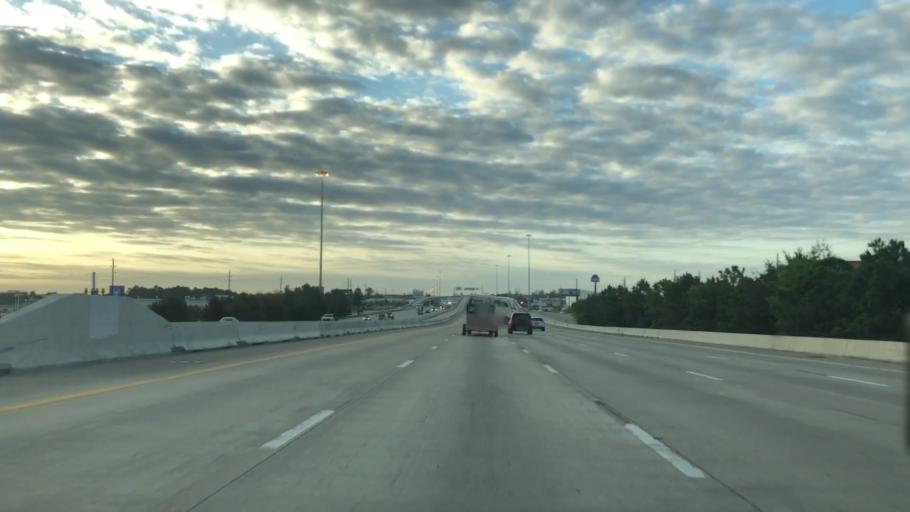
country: US
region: Texas
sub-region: Harris County
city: Spring
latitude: 30.0193
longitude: -95.4288
